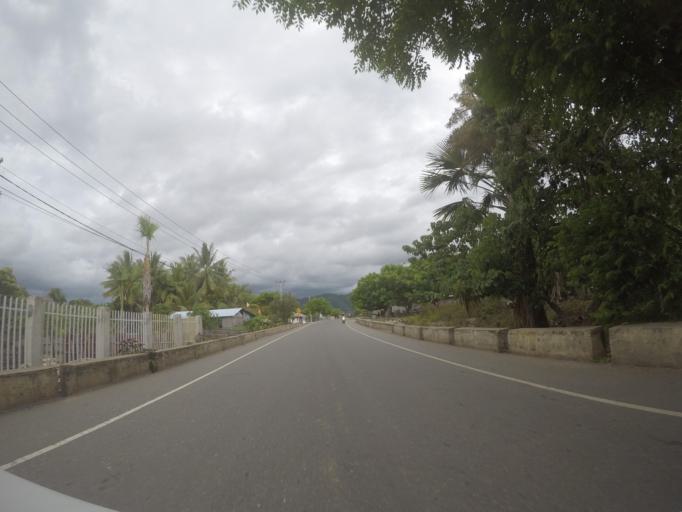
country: TL
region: Liquica
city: Maubara
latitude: -8.7804
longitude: 125.1013
